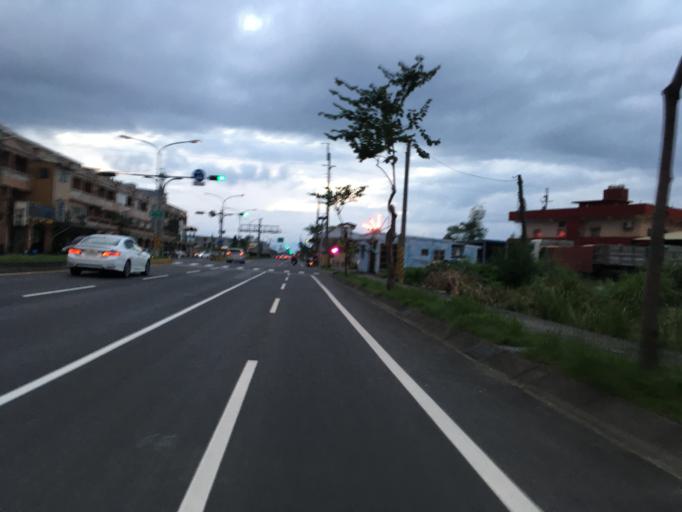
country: TW
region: Taiwan
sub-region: Yilan
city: Yilan
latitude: 24.6218
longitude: 121.8404
